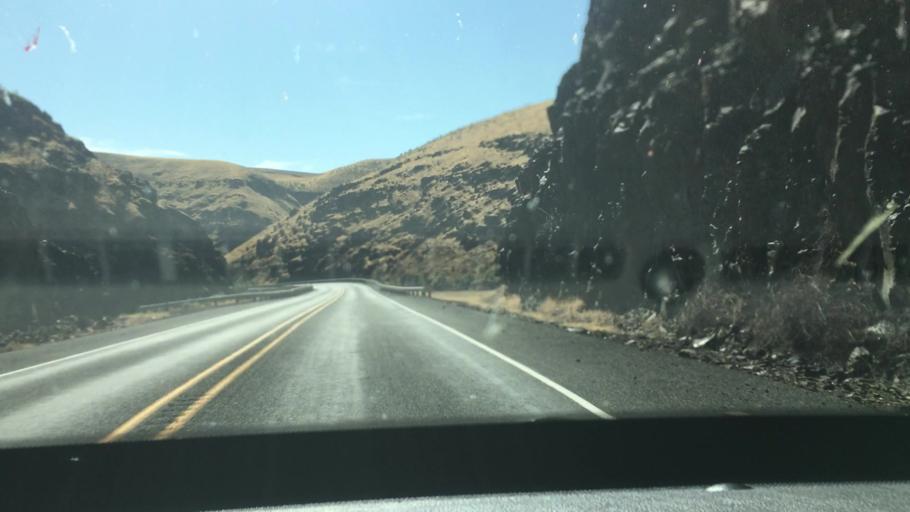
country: US
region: Washington
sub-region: Klickitat County
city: Goldendale
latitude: 45.6479
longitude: -120.8011
